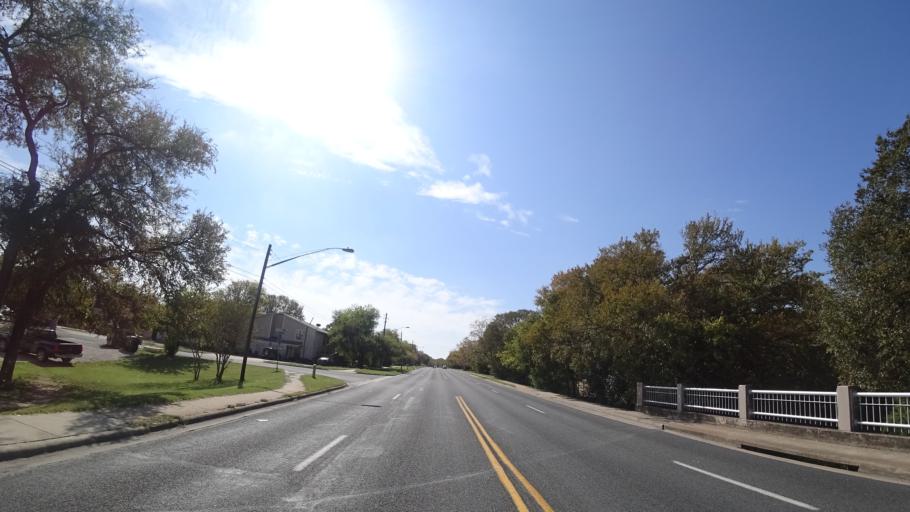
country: US
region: Texas
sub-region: Travis County
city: Rollingwood
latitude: 30.2241
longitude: -97.8048
